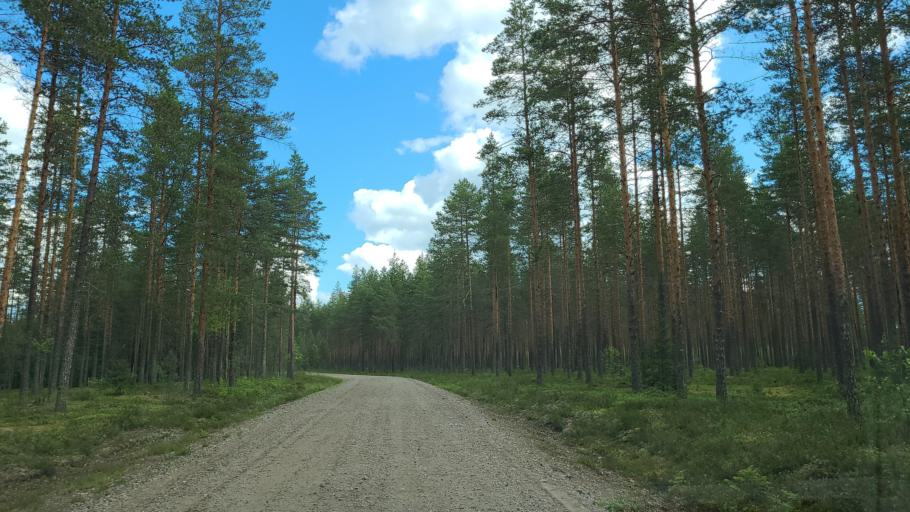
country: FI
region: Northern Savo
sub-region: Koillis-Savo
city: Kaavi
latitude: 63.0541
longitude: 28.8221
